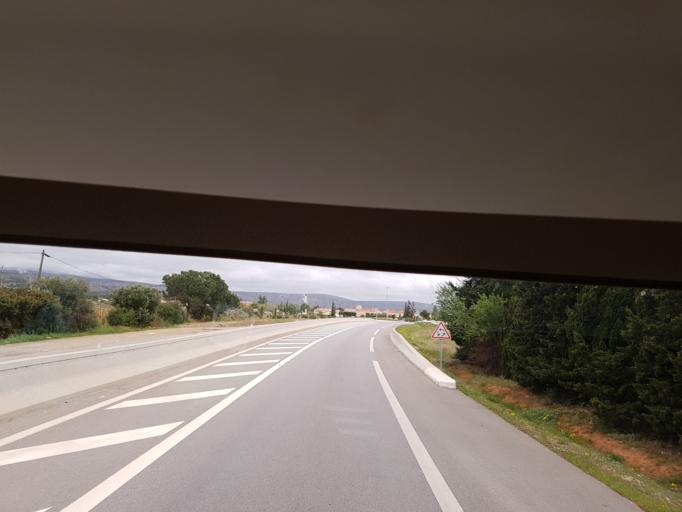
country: FR
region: Languedoc-Roussillon
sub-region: Departement des Pyrenees-Orientales
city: Salses-le-Chateau
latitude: 42.8215
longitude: 2.9164
